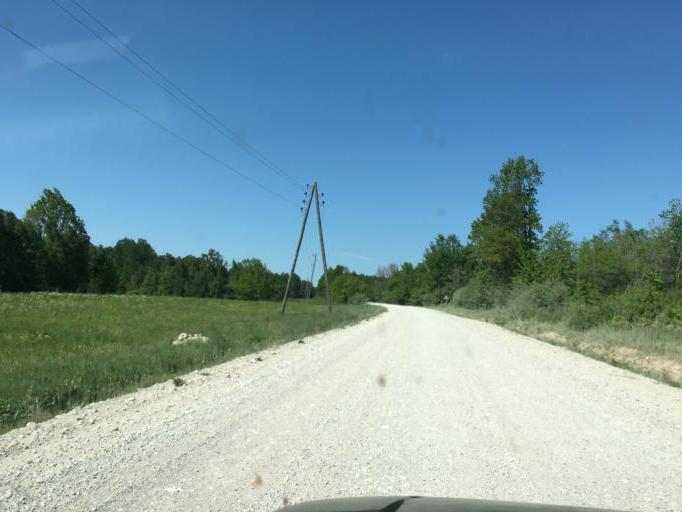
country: LV
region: Dundaga
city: Dundaga
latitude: 57.4480
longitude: 22.3215
